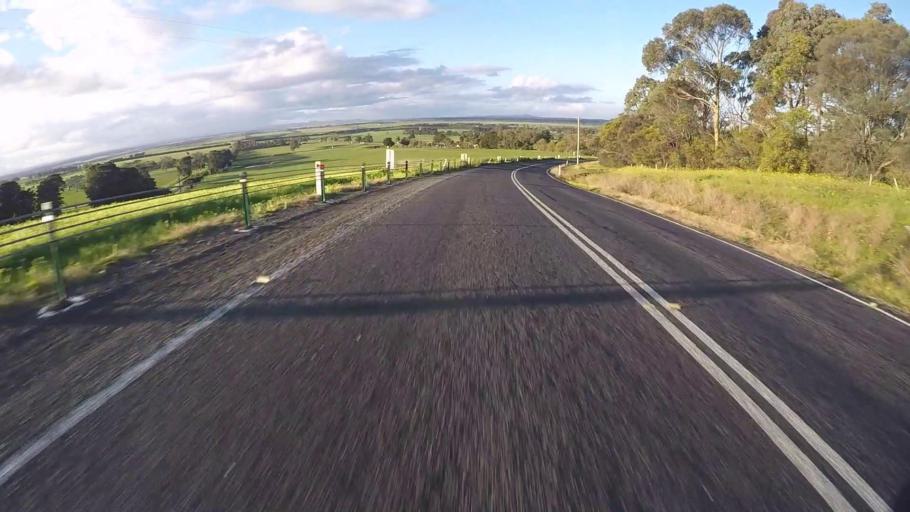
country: AU
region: Victoria
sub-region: Greater Geelong
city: Wandana Heights
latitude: -38.1557
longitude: 144.1637
